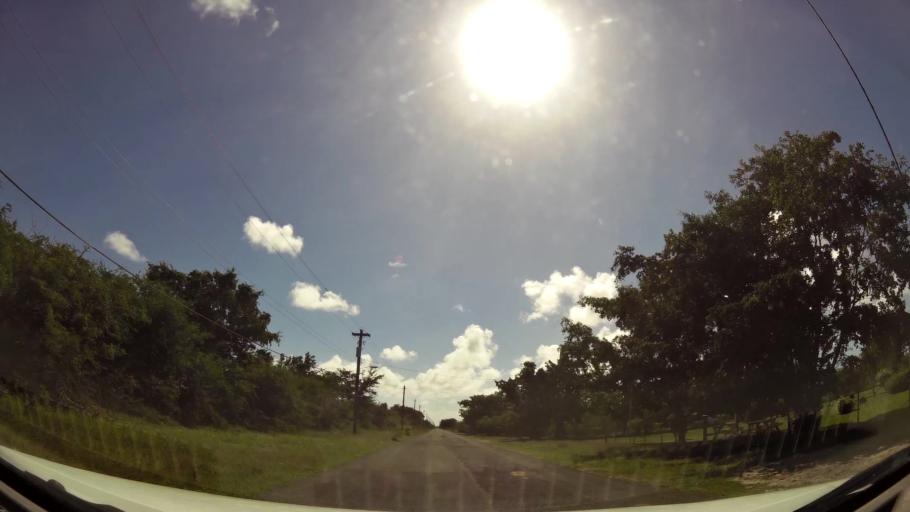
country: AG
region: Barbuda
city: Codrington
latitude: 17.6132
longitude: -61.8285
